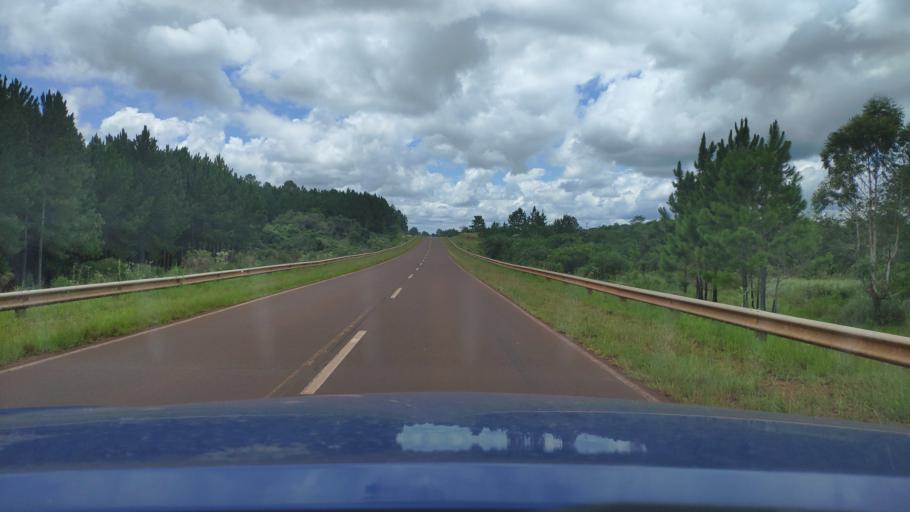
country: AR
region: Misiones
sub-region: Departamento de San Javier
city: San Javier
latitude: -27.8499
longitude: -55.2455
